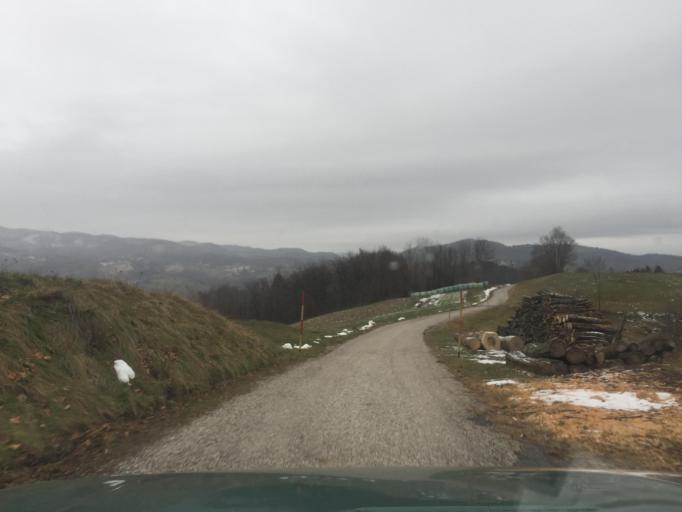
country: SI
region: Kanal
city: Kanal
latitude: 46.0709
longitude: 13.6933
